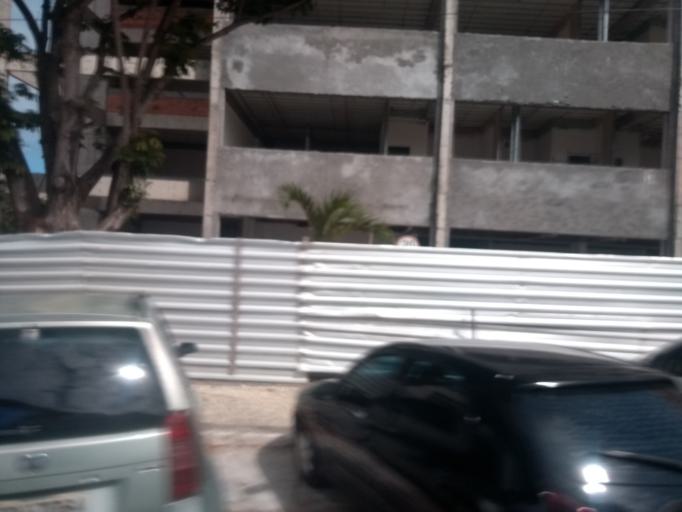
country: BR
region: Bahia
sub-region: Salvador
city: Salvador
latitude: -12.9448
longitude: -38.4249
